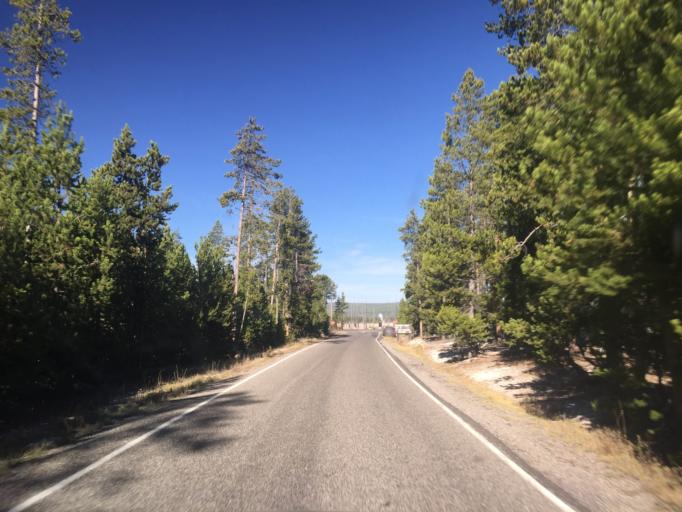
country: US
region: Montana
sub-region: Gallatin County
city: West Yellowstone
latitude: 44.5478
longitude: -110.8052
